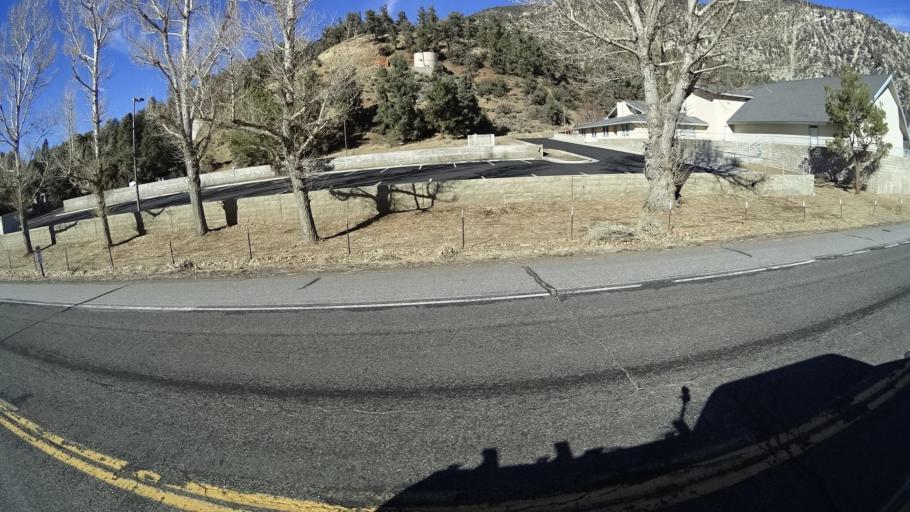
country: US
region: California
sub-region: Kern County
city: Frazier Park
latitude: 34.8184
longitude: -118.9933
